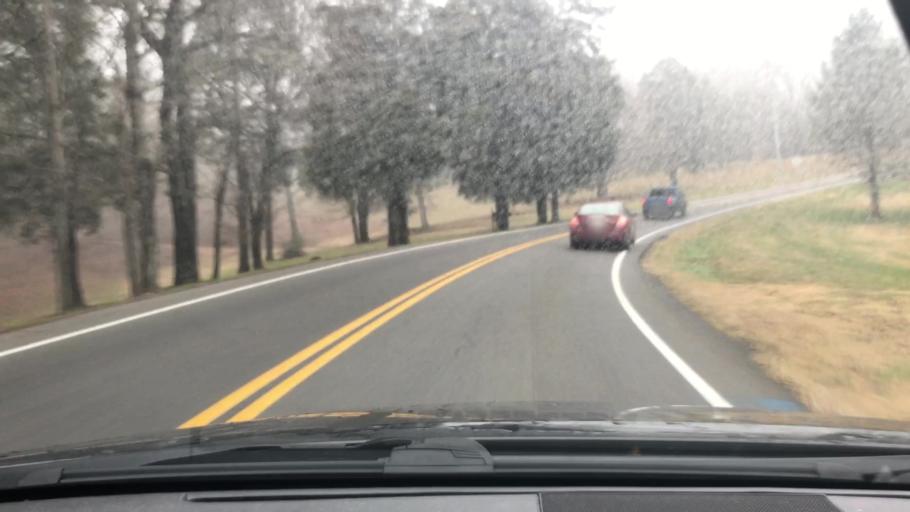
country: US
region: Tennessee
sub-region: Cheatham County
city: Ashland City
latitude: 36.2835
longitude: -87.1819
